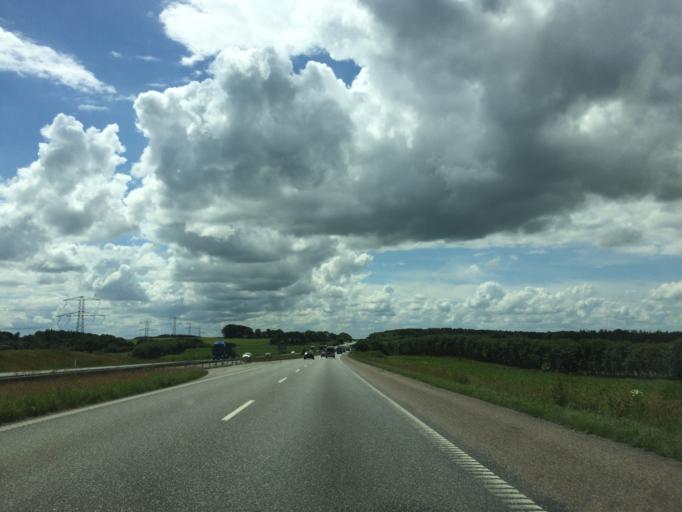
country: DK
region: North Denmark
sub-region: Rebild Kommune
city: Stovring
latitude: 56.8501
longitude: 9.7567
